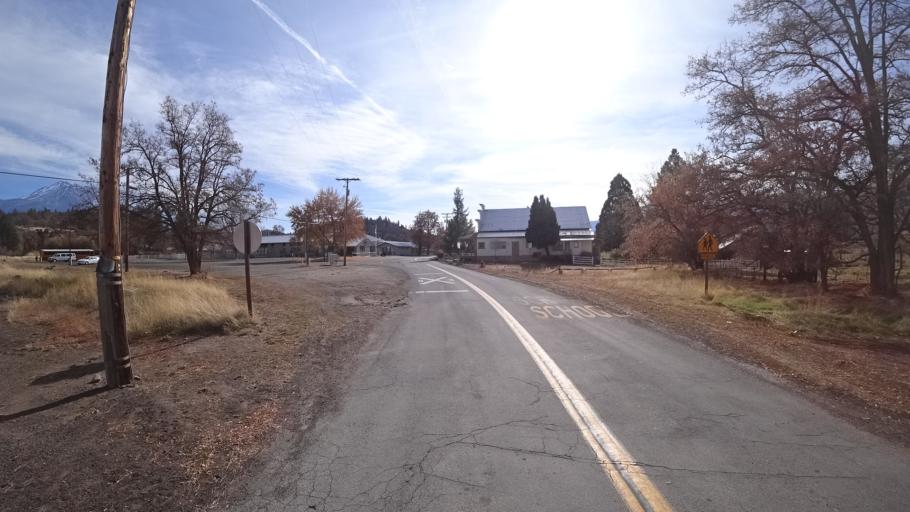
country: US
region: California
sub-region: Siskiyou County
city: Weed
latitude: 41.4582
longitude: -122.4324
